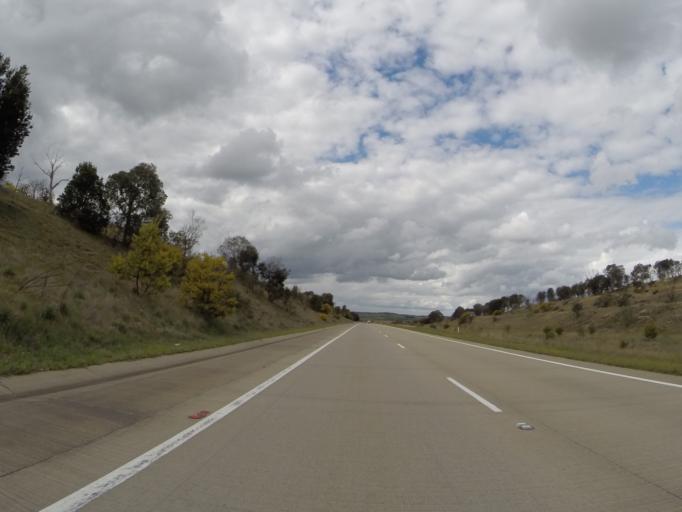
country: AU
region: New South Wales
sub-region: Yass Valley
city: Gundaroo
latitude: -34.8187
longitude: 149.4081
